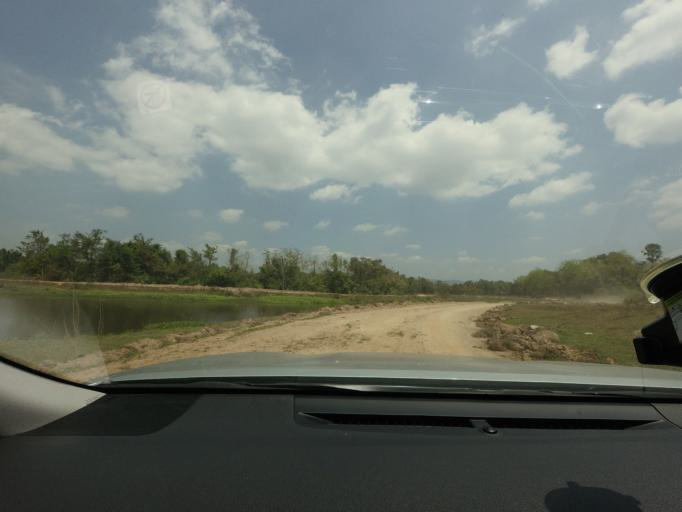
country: TH
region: Narathiwat
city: Rueso
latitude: 6.3886
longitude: 101.4986
